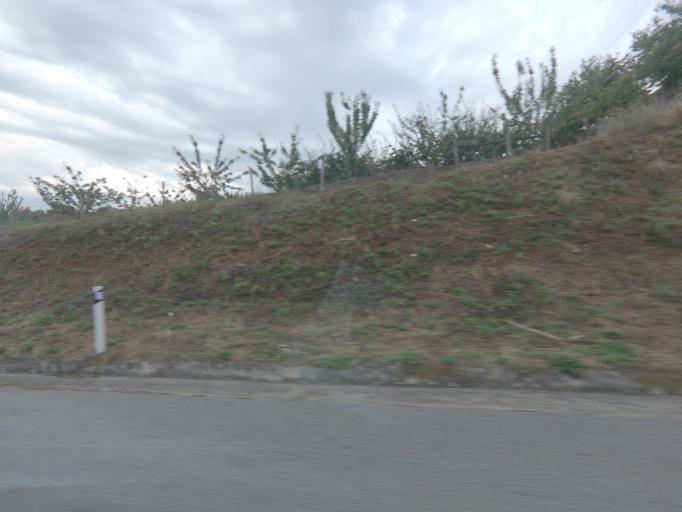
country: PT
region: Viseu
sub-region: Lamego
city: Lamego
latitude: 41.0772
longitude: -7.8060
